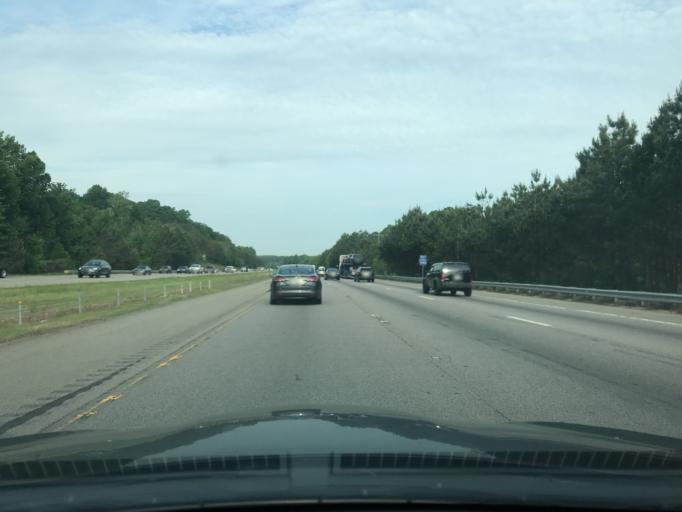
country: US
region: North Carolina
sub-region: Wake County
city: West Raleigh
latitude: 35.9160
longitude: -78.6924
